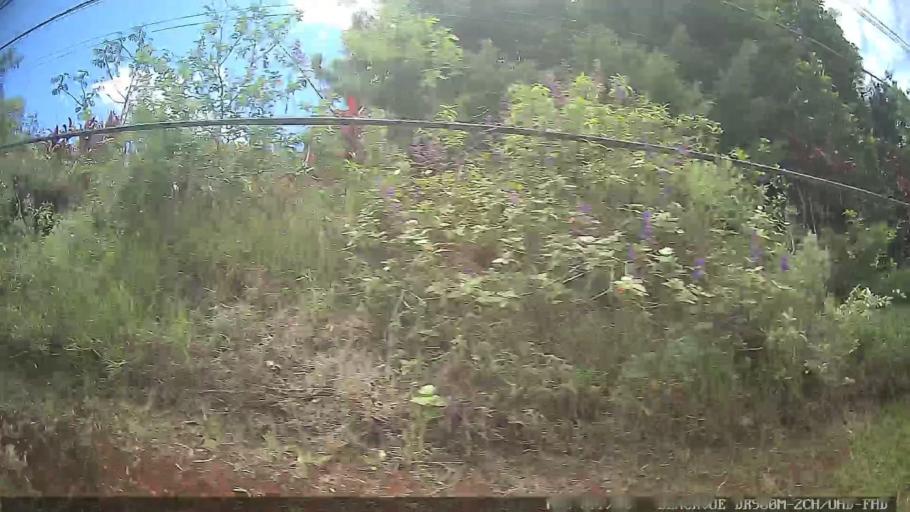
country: BR
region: Sao Paulo
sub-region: Biritiba-Mirim
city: Biritiba Mirim
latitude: -23.5395
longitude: -45.9122
